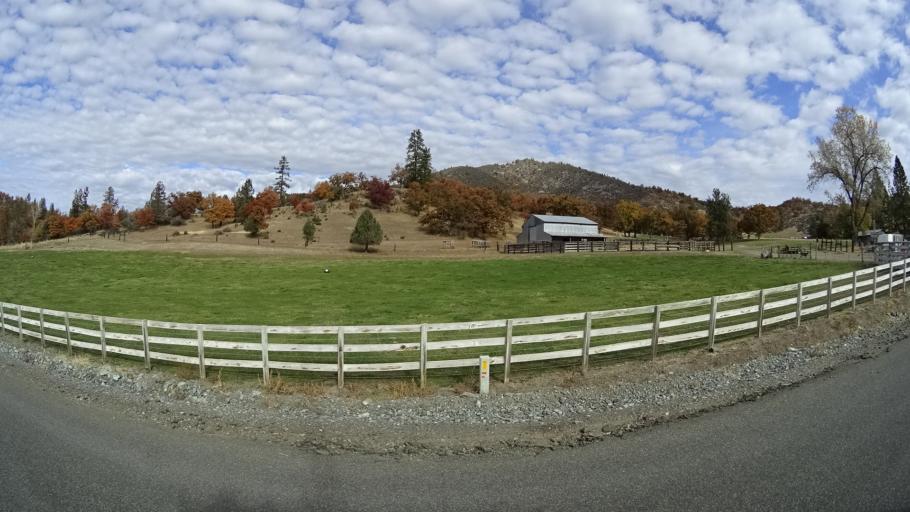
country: US
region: California
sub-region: Siskiyou County
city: Yreka
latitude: 41.6248
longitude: -122.7846
